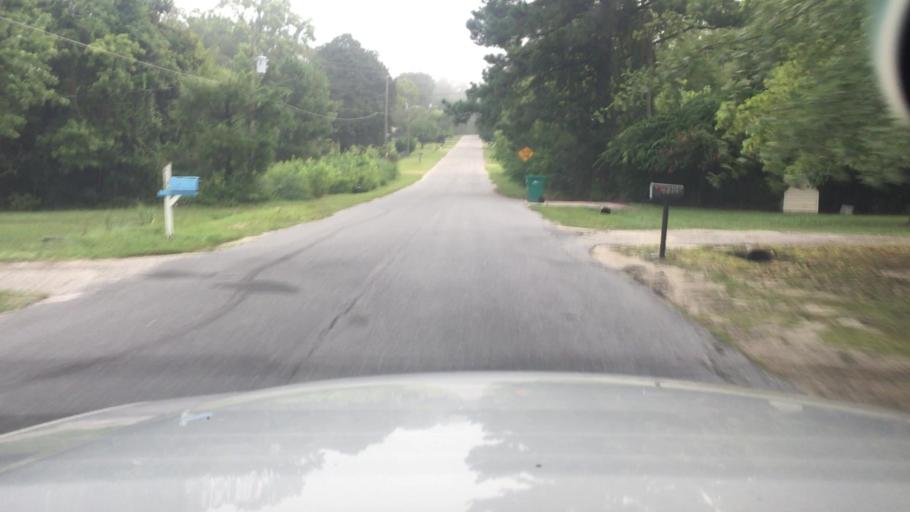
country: US
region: North Carolina
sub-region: Cumberland County
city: Hope Mills
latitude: 35.0166
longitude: -78.9387
